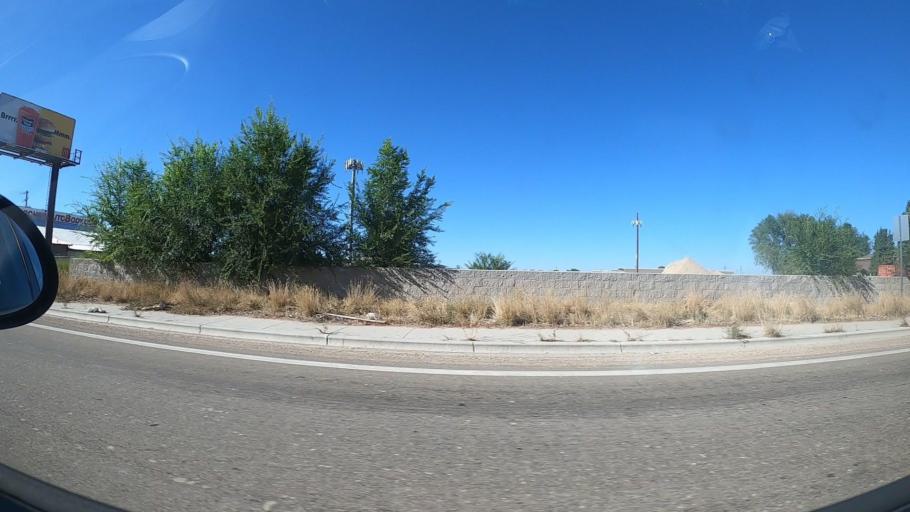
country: US
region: Idaho
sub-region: Canyon County
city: Nampa
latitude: 43.6051
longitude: -116.6055
